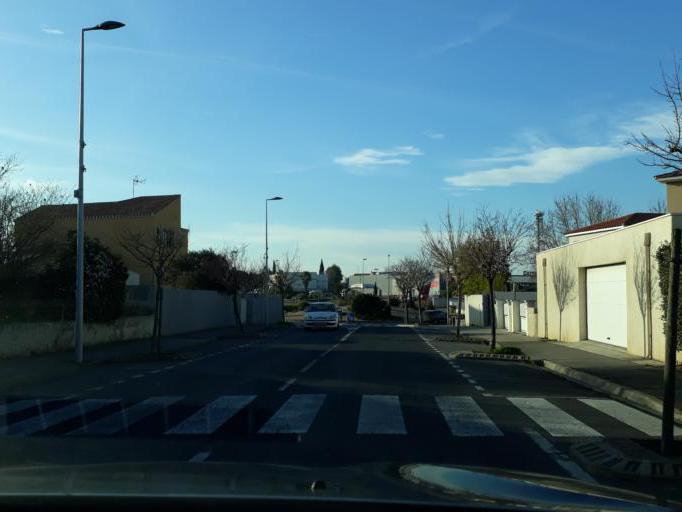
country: FR
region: Languedoc-Roussillon
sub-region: Departement de l'Herault
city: Marseillan
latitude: 43.3547
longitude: 3.5218
